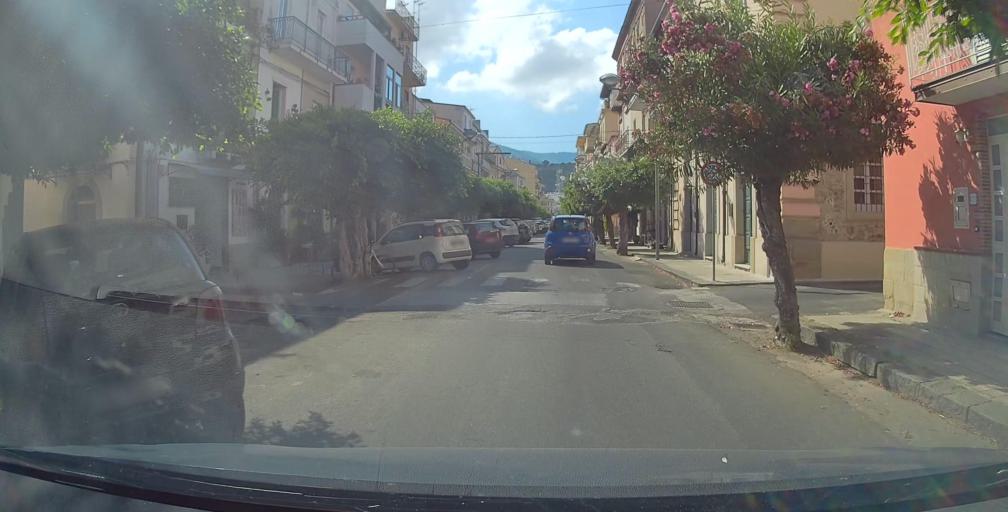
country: IT
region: Sicily
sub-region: Messina
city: Patti
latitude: 38.1522
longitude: 14.9691
